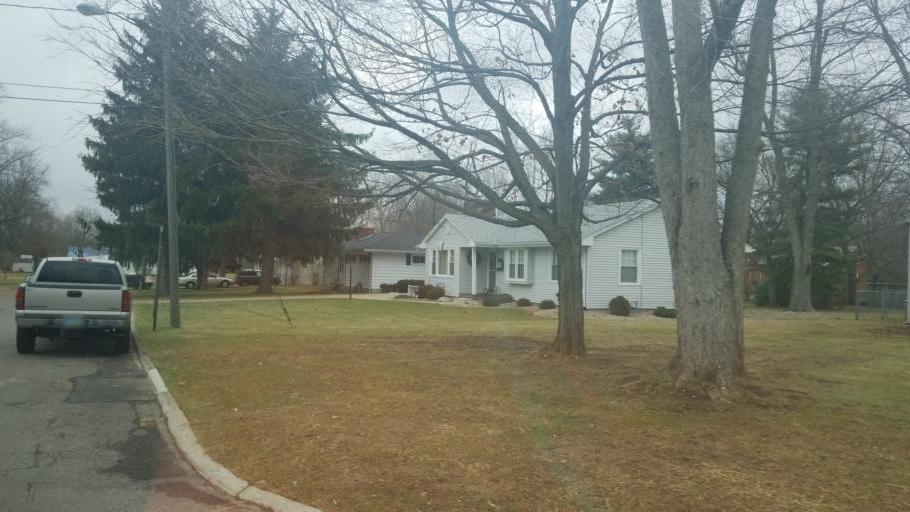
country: US
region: Ohio
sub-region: Crawford County
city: Galion
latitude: 40.7437
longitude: -82.7898
